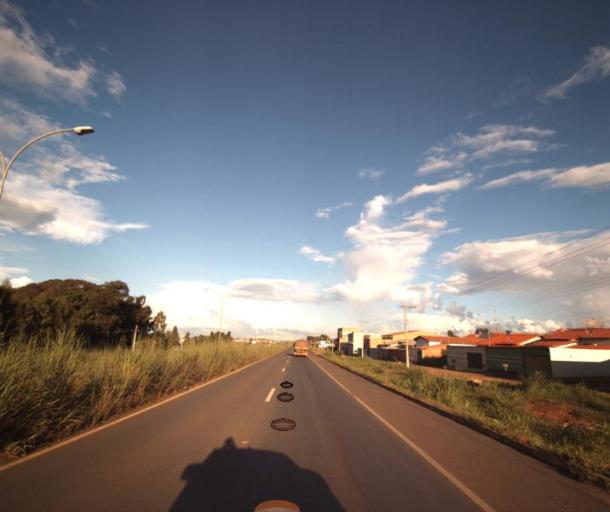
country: BR
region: Goias
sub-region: Anapolis
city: Anapolis
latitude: -16.2844
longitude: -48.9510
